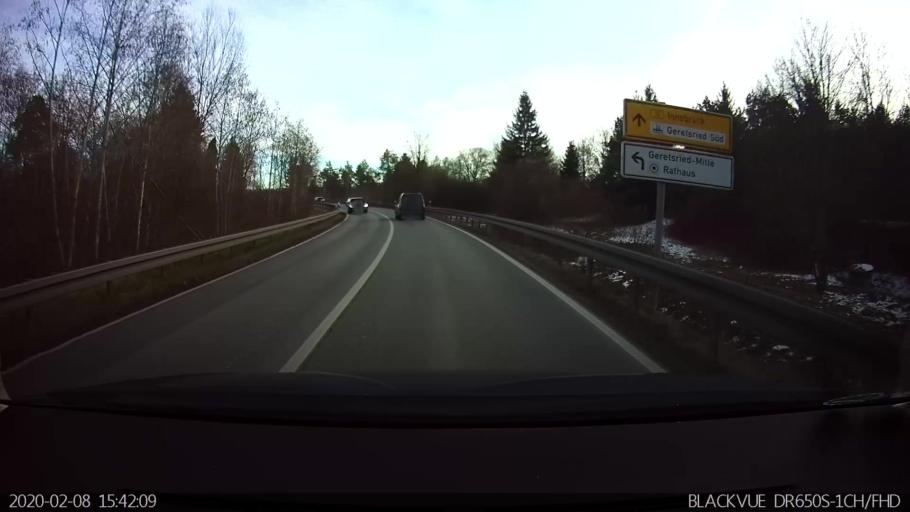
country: DE
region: Bavaria
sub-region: Upper Bavaria
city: Geretsried
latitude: 47.8753
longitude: 11.4620
